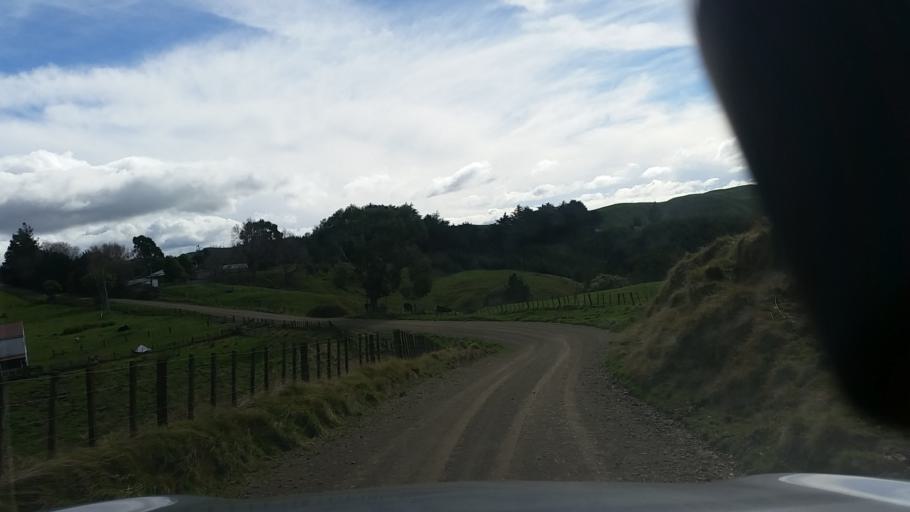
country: NZ
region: Hawke's Bay
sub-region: Napier City
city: Napier
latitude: -39.2302
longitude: 176.9897
